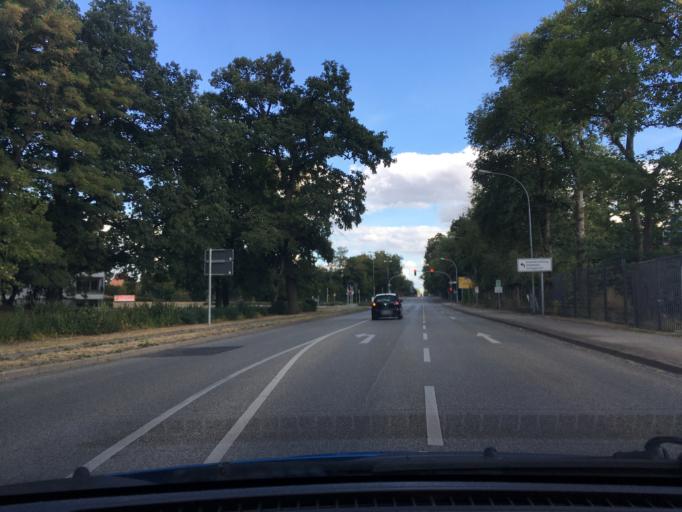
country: DE
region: Mecklenburg-Vorpommern
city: Ludwigslust
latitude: 53.3209
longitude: 11.4983
